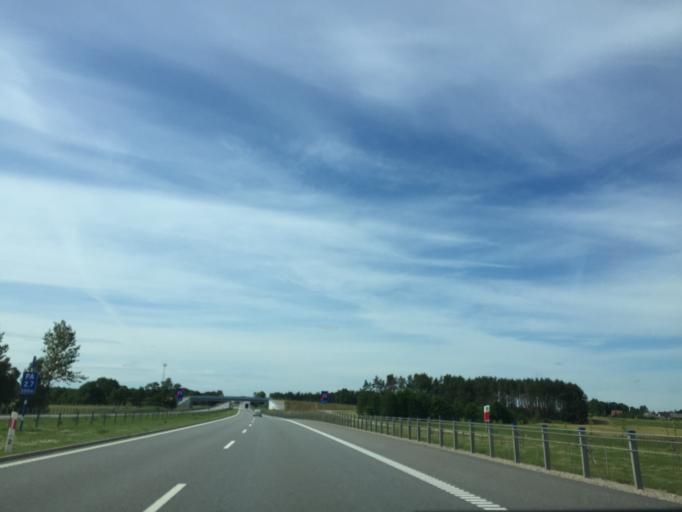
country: PL
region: Podlasie
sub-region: Powiat suwalski
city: Raczki
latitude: 53.9908
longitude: 22.8077
